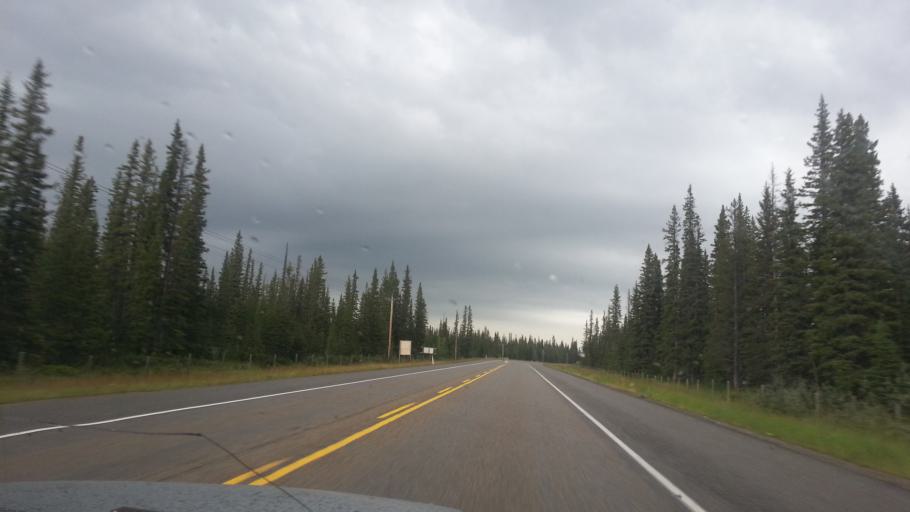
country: CA
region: Alberta
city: Cochrane
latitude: 50.9589
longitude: -114.5525
